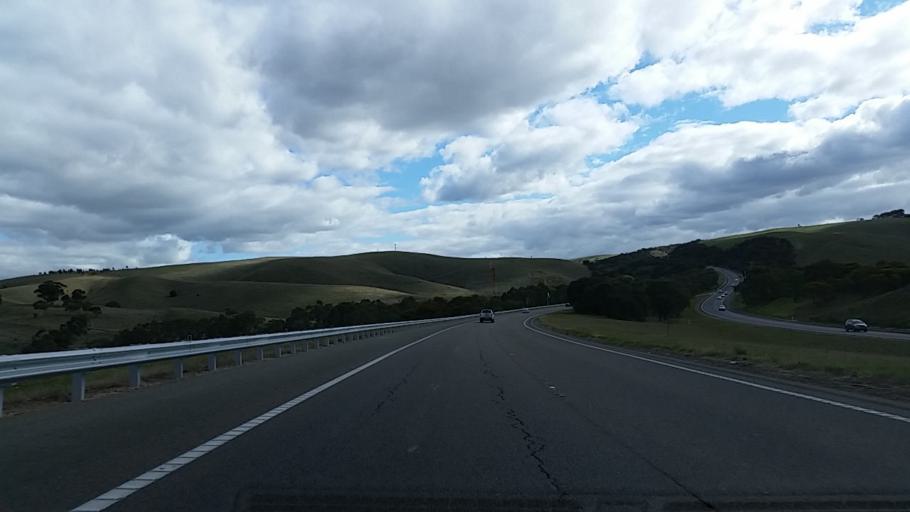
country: AU
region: South Australia
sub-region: Mount Barker
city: Callington
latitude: -35.1156
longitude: 138.9939
